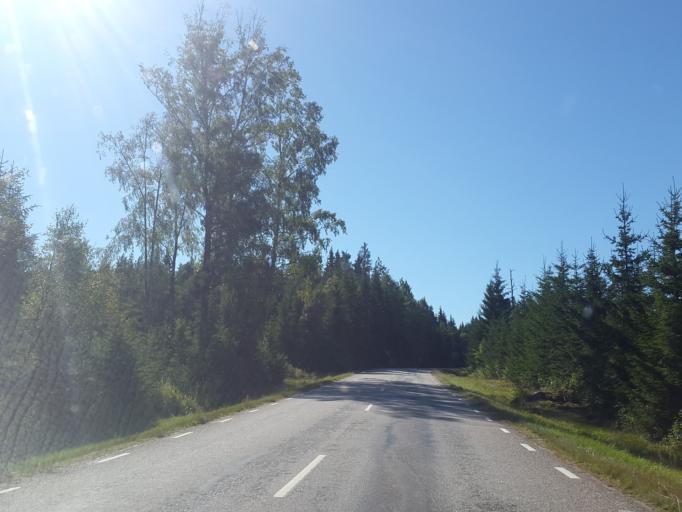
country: SE
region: Vaestra Goetaland
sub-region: Herrljunga Kommun
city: Herrljunga
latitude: 57.9681
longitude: 13.0036
